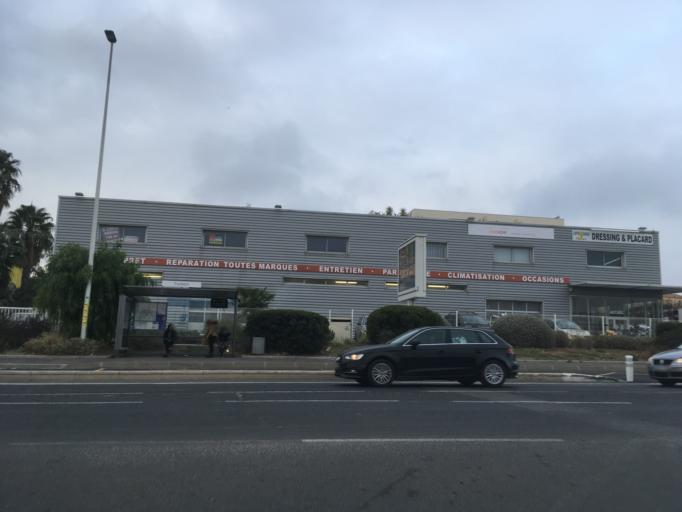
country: FR
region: Languedoc-Roussillon
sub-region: Departement de l'Herault
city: Lattes
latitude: 43.5790
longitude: 3.8780
